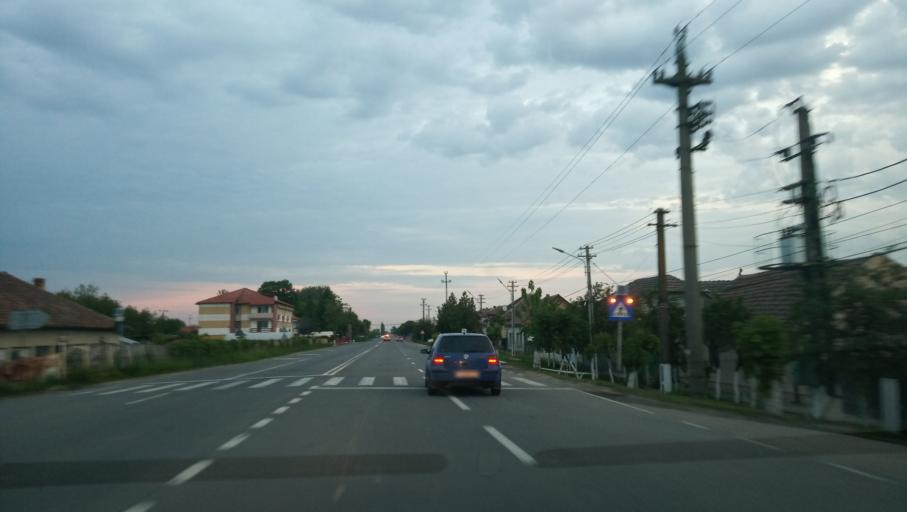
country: RO
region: Timis
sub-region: Comuna Sag
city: Sag
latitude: 45.6472
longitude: 21.1750
